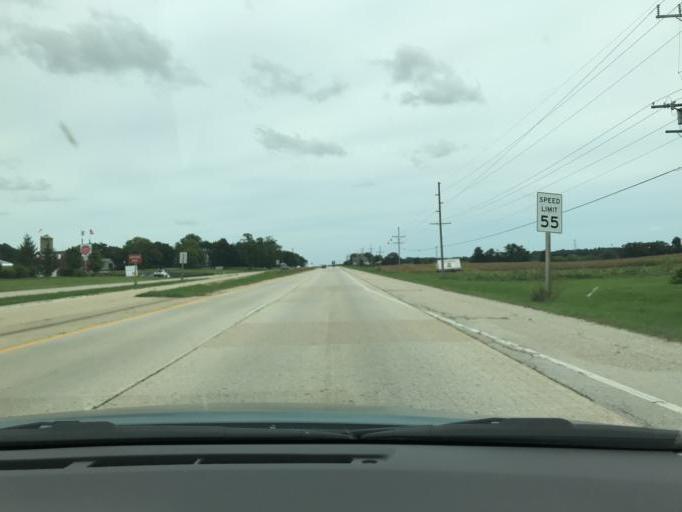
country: US
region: Wisconsin
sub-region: Kenosha County
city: Pleasant Prairie
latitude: 42.5672
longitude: -87.9815
